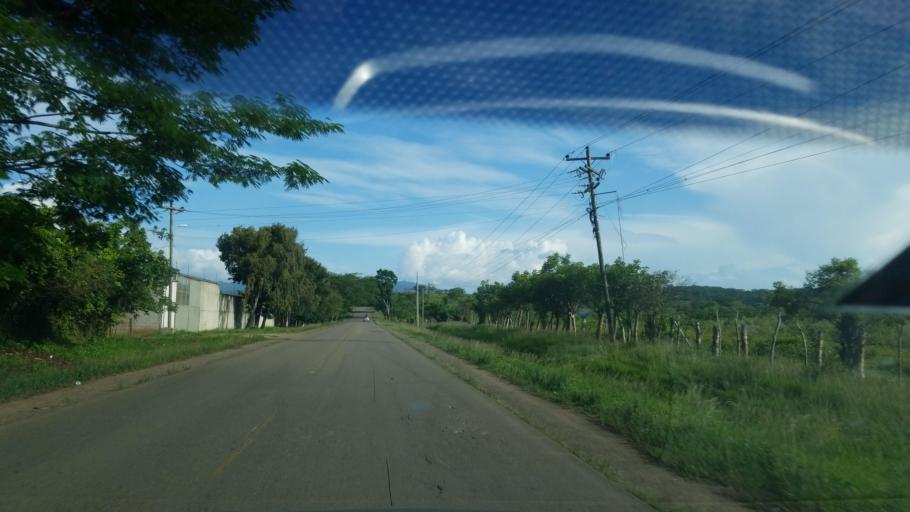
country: HN
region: El Paraiso
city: Arauli
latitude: 13.9326
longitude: -86.5583
